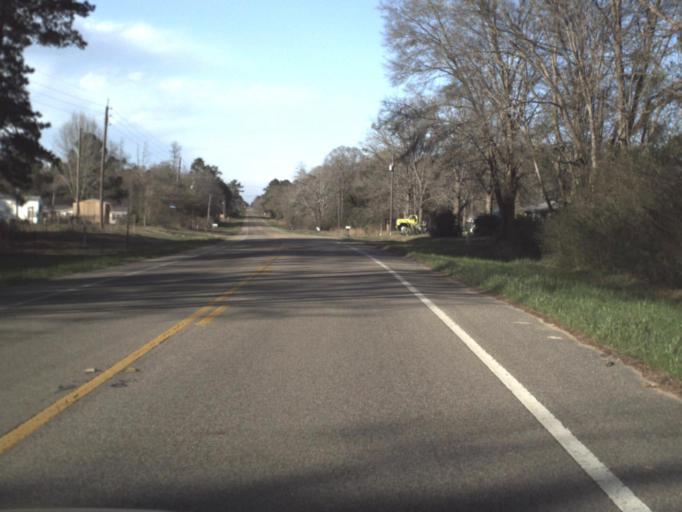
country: US
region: Florida
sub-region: Jackson County
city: Marianna
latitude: 30.7061
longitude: -85.2309
